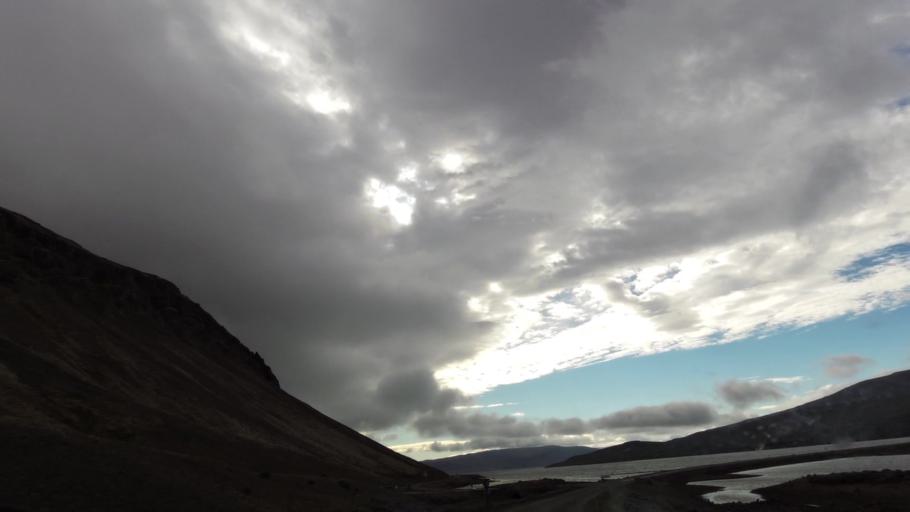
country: IS
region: West
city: Olafsvik
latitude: 65.5306
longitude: -23.7802
